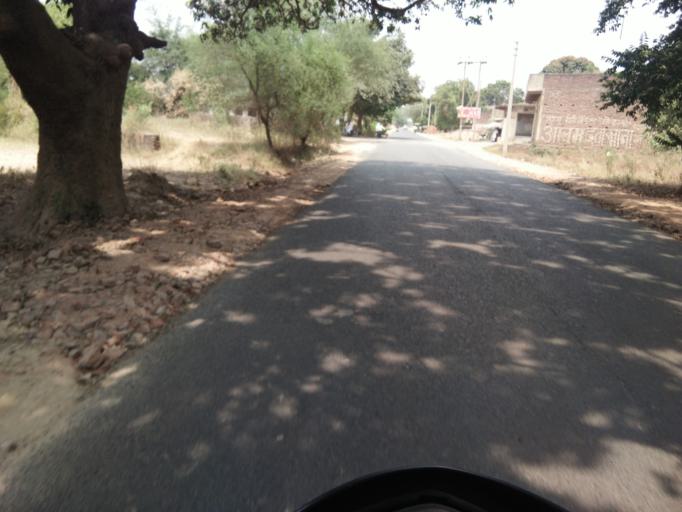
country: IN
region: Uttar Pradesh
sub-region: Ghazipur
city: Zamania
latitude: 25.4376
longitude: 83.6835
